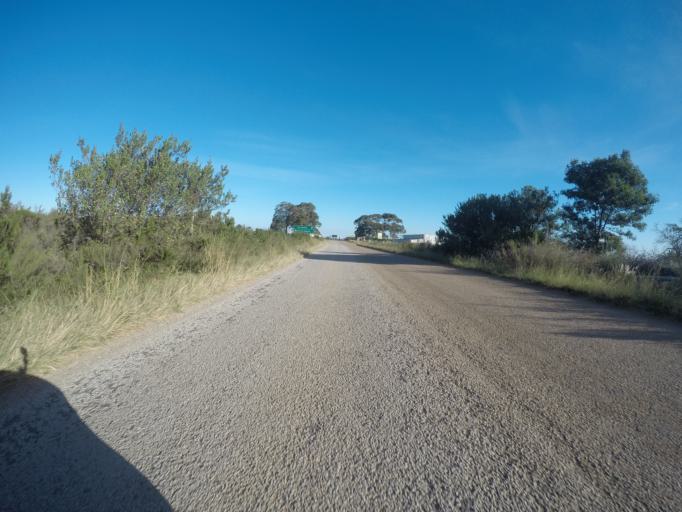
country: ZA
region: Eastern Cape
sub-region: Cacadu District Municipality
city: Kareedouw
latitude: -34.0031
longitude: 24.2342
